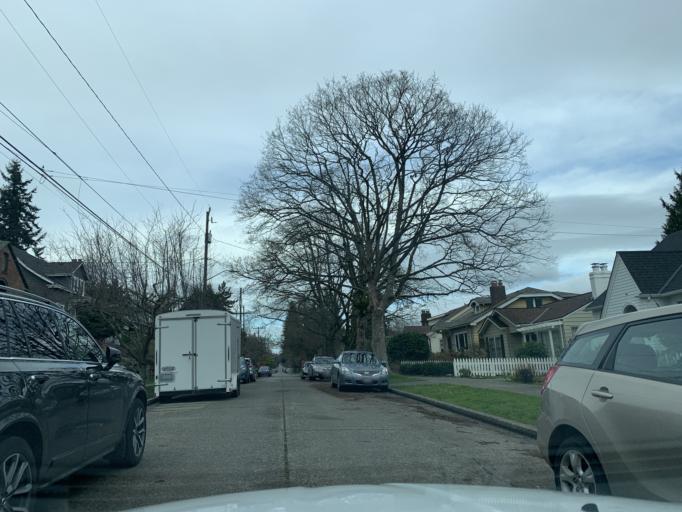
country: US
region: Washington
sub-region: King County
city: Yarrow Point
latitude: 47.6674
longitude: -122.2868
